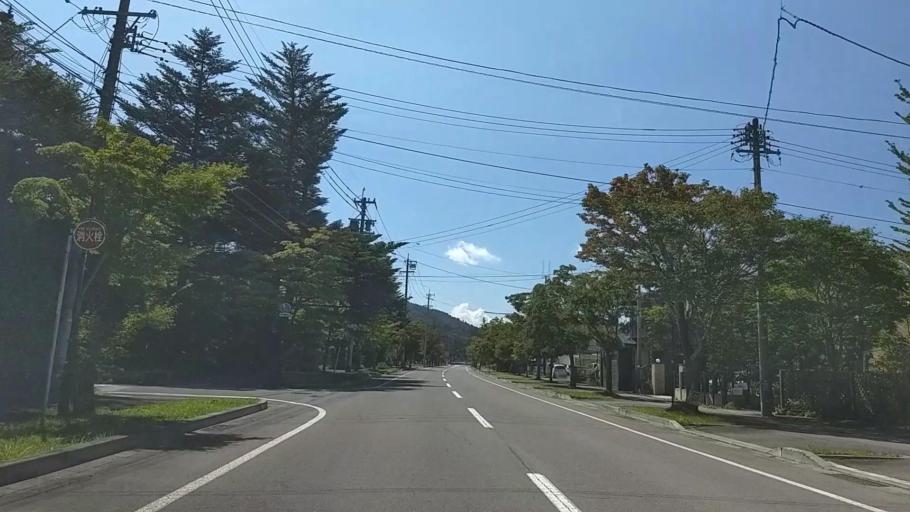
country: JP
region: Nagano
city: Saku
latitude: 36.3471
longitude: 138.6389
